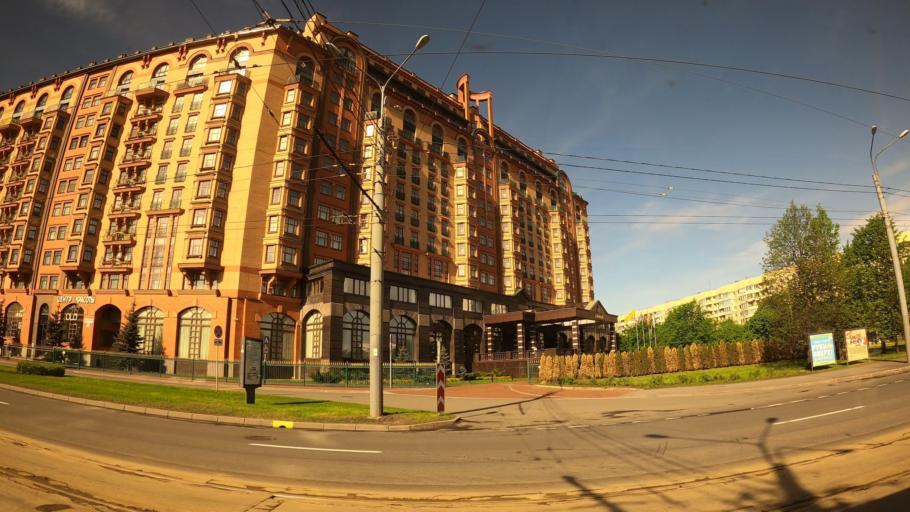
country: RU
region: St.-Petersburg
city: Vasyl'evsky Ostrov
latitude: 59.9421
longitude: 30.2315
